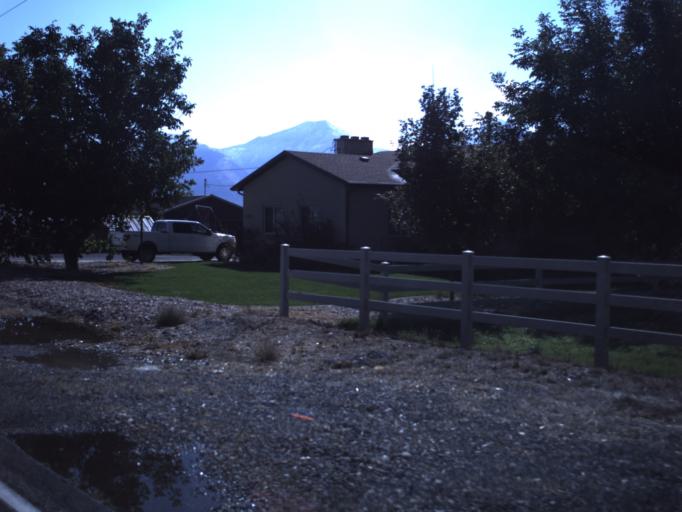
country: US
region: Utah
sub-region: Utah County
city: Benjamin
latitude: 40.0983
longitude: -111.7098
